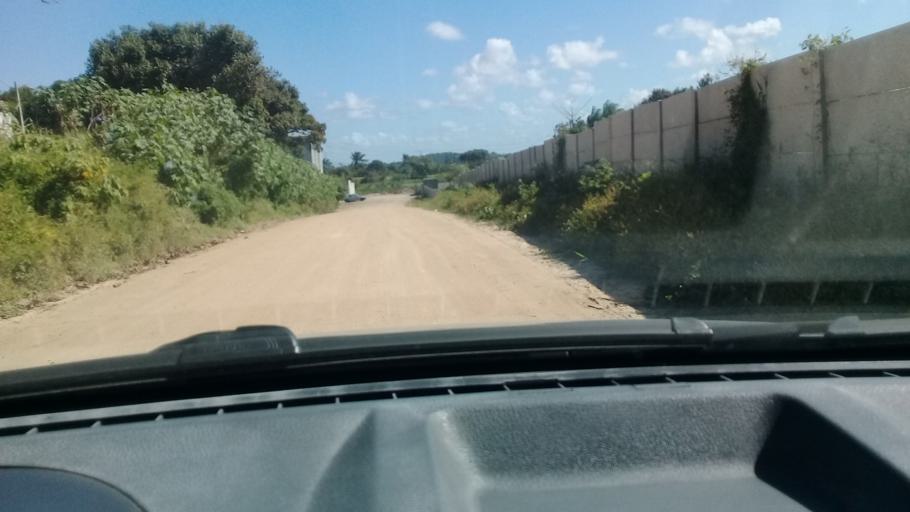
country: BR
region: Pernambuco
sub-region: Jaboatao Dos Guararapes
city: Jaboatao
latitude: -8.1516
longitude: -34.9502
